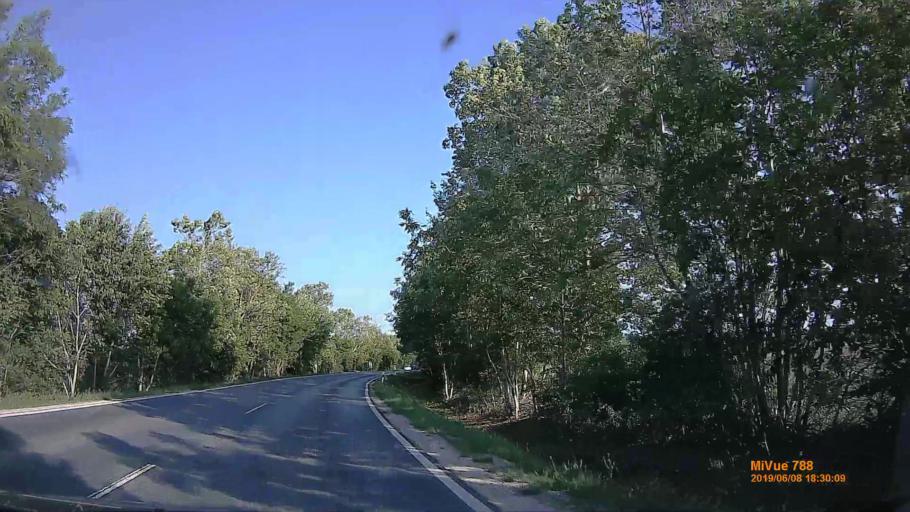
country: HU
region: Vas
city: Buk
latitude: 47.3776
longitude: 16.8829
